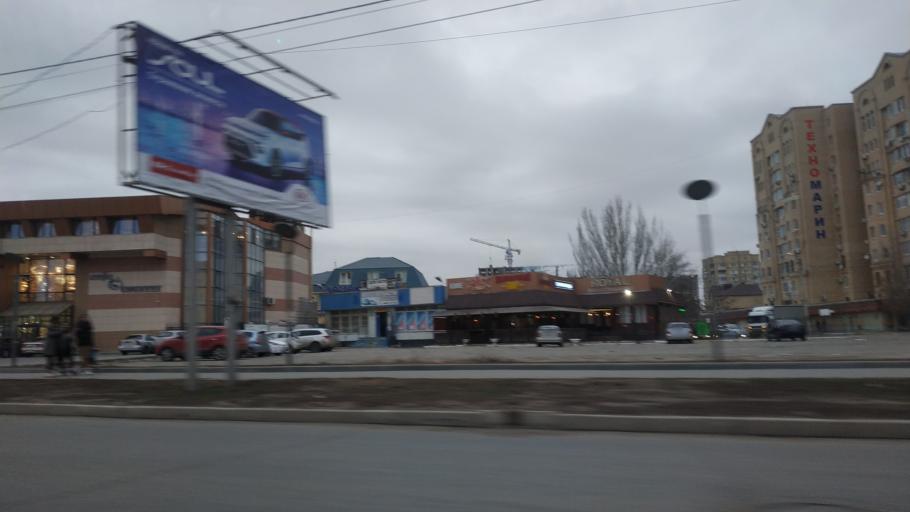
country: RU
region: Astrakhan
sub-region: Gorod Astrakhan'
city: Astrakhan'
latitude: 46.3331
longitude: 48.0130
